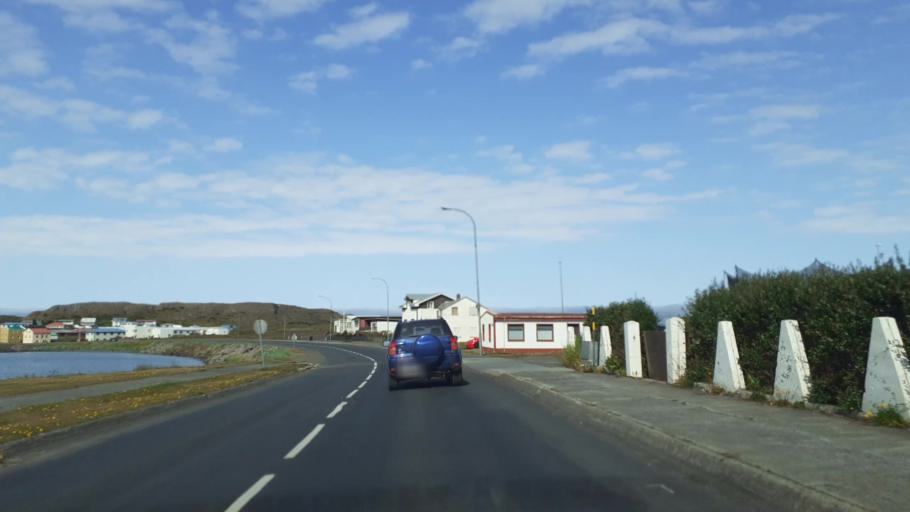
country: IS
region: Northwest
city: Saudarkrokur
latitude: 65.8251
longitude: -20.3073
